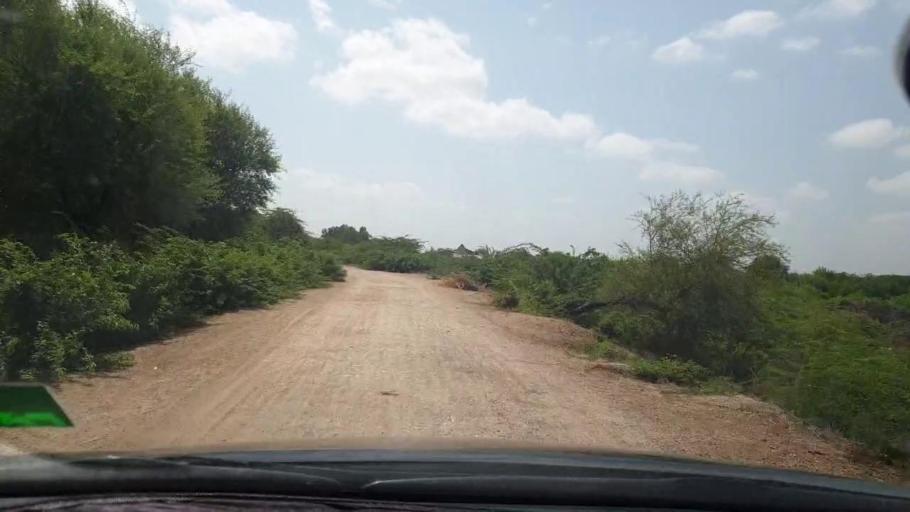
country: PK
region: Sindh
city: Tando Bago
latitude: 24.8699
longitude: 69.0858
